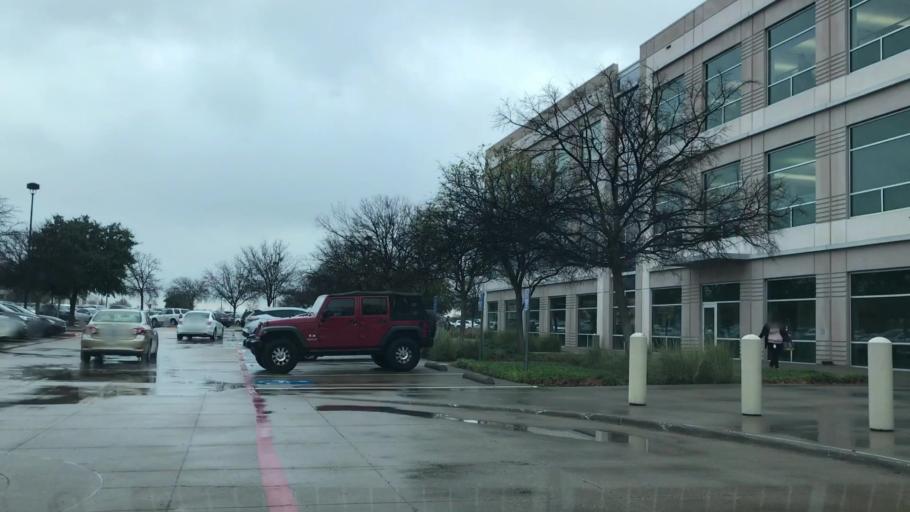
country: US
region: Texas
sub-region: Dallas County
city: Farmers Branch
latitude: 32.8983
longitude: -96.9499
